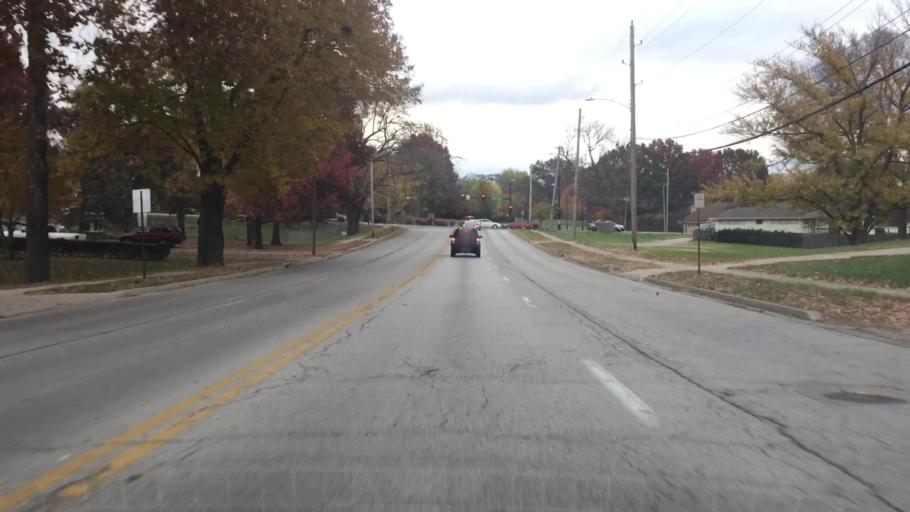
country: US
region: Missouri
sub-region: Jackson County
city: Raytown
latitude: 38.9943
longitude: -94.4657
